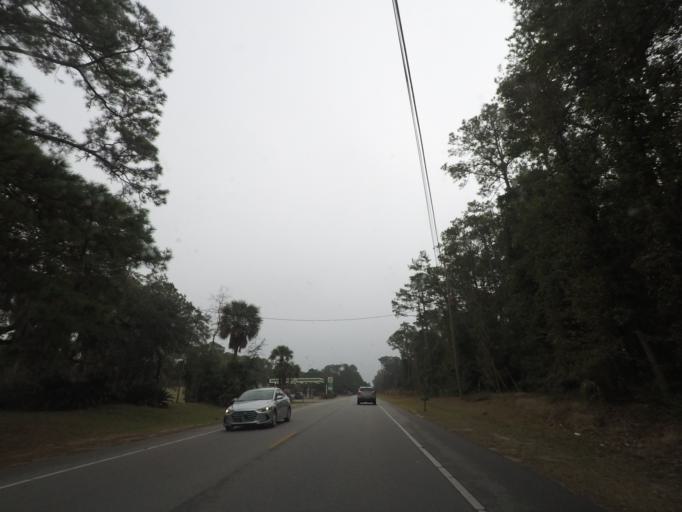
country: US
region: South Carolina
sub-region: Charleston County
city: Seabrook Island
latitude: 32.5175
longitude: -80.2998
